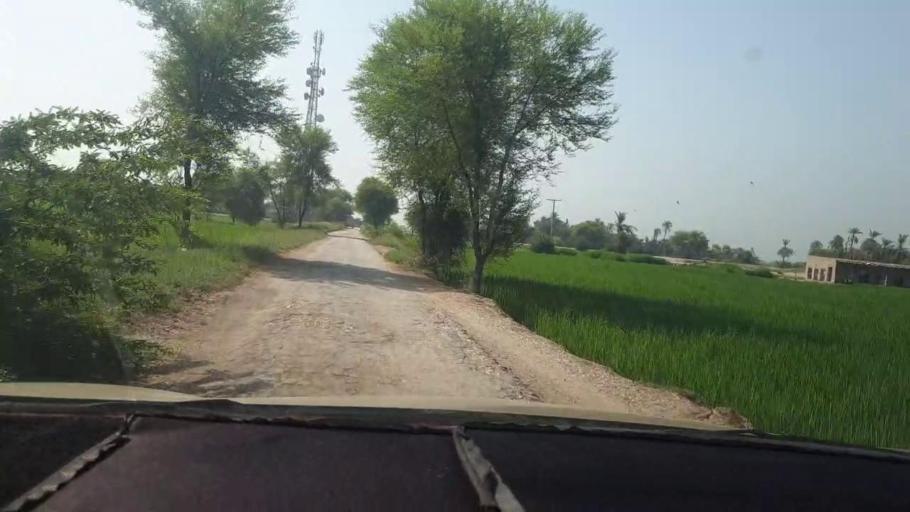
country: PK
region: Sindh
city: Kambar
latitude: 27.5610
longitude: 68.0587
